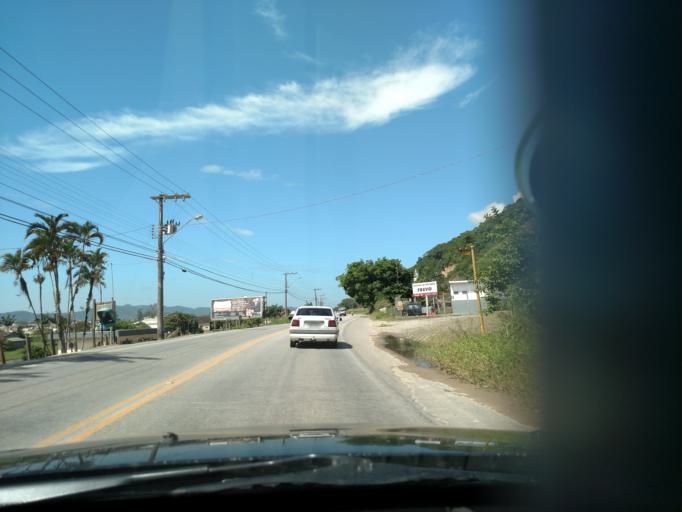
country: BR
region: Santa Catarina
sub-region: Itajai
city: Itajai
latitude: -26.8879
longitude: -48.7537
